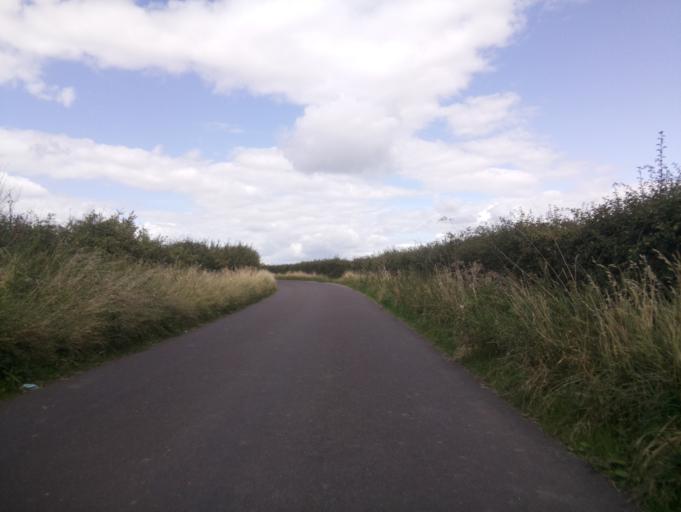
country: GB
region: England
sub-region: Wiltshire
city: Bratton
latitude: 51.2855
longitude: -2.1284
